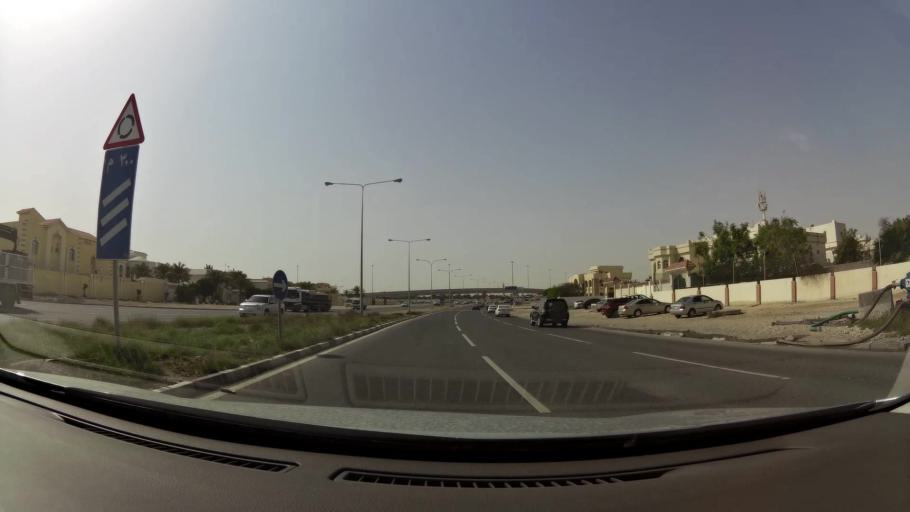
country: QA
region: Baladiyat ad Dawhah
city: Doha
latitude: 25.2404
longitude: 51.5241
